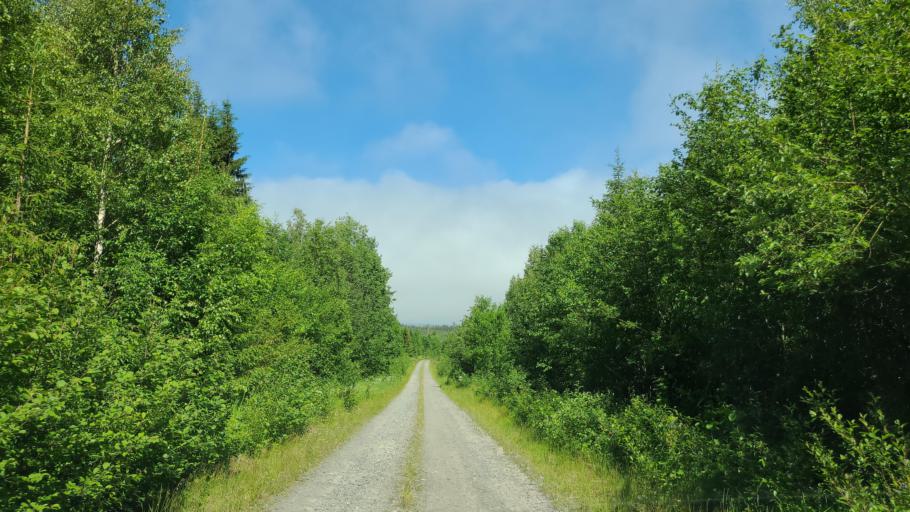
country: SE
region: Vaesternorrland
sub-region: OErnskoeldsviks Kommun
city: Husum
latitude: 63.4518
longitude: 19.2384
